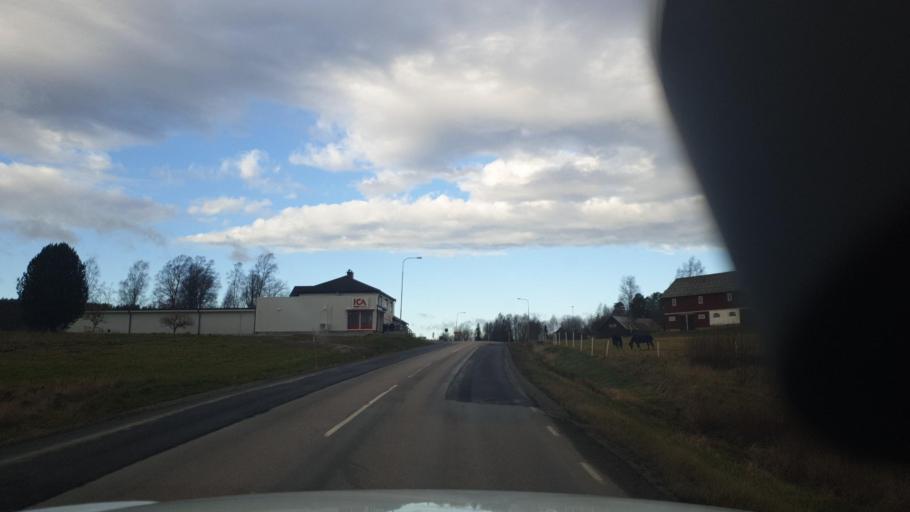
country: SE
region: Vaermland
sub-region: Arvika Kommun
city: Arvika
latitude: 59.7943
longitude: 12.6114
